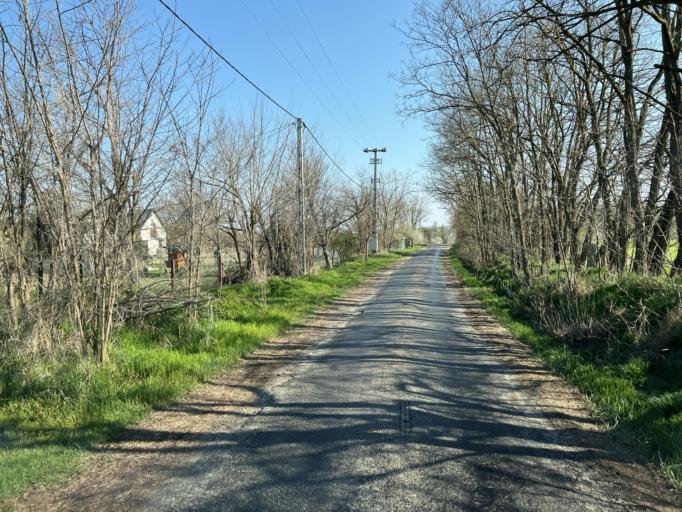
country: SK
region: Nitriansky
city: Sahy
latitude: 47.9887
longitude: 18.8143
